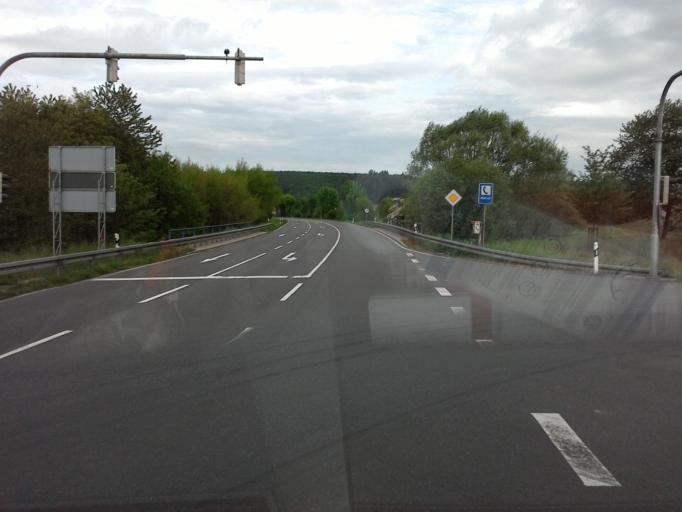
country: DE
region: Bavaria
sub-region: Regierungsbezirk Unterfranken
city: Kreuzwertheim
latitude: 49.7711
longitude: 9.5735
